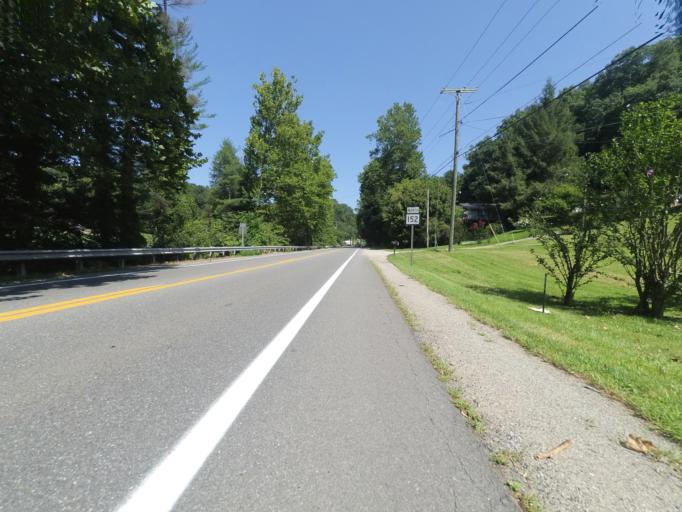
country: US
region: West Virginia
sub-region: Cabell County
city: Huntington
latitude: 38.3802
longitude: -82.4561
